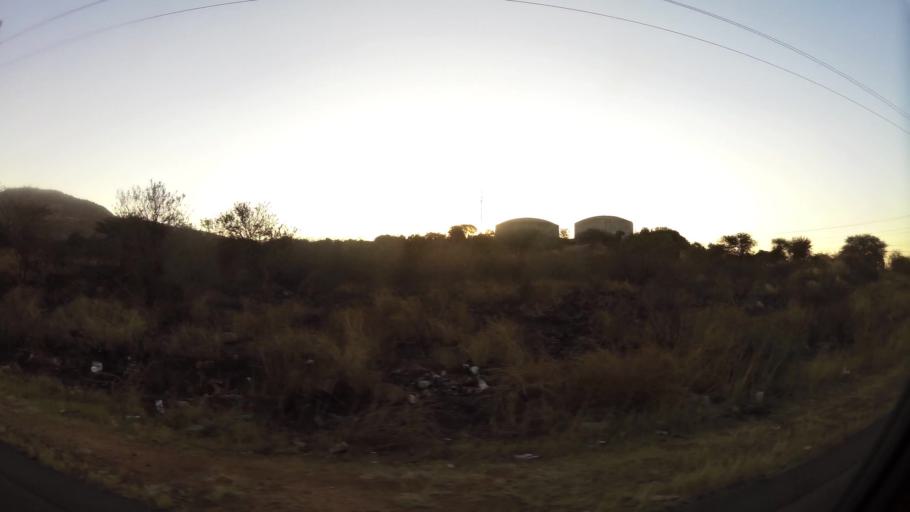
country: ZA
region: North-West
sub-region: Bojanala Platinum District Municipality
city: Rustenburg
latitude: -25.6336
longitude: 27.2022
